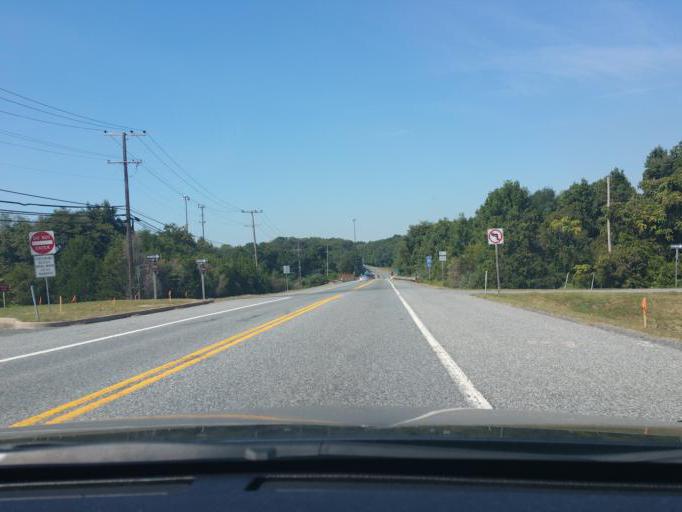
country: US
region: Maryland
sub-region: Harford County
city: Havre de Grace
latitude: 39.5702
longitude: -76.1352
